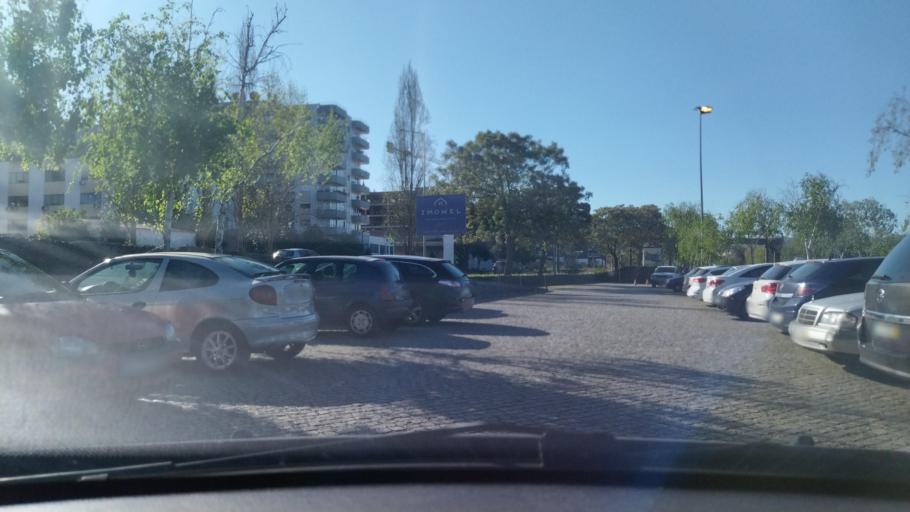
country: PT
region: Coimbra
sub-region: Coimbra
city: Coimbra
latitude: 40.2030
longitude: -8.4251
